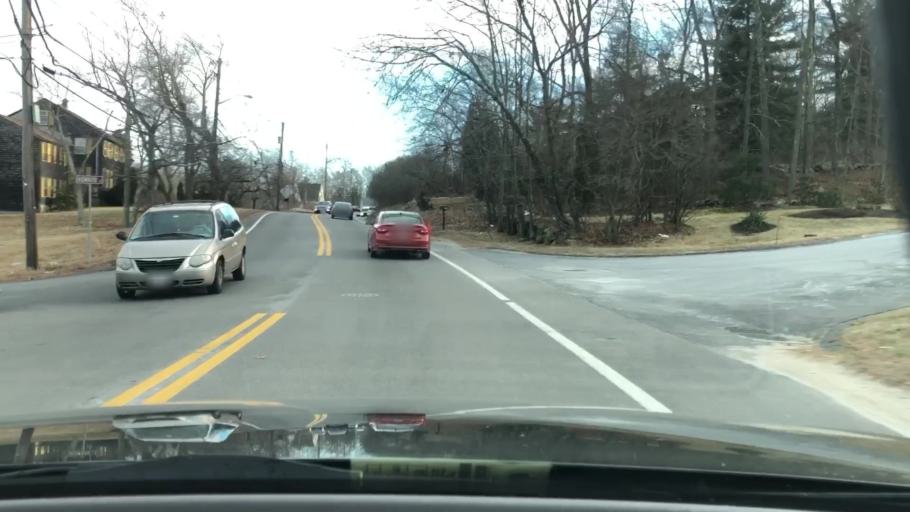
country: US
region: Massachusetts
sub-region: Worcester County
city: Milford
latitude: 42.1242
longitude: -71.5165
